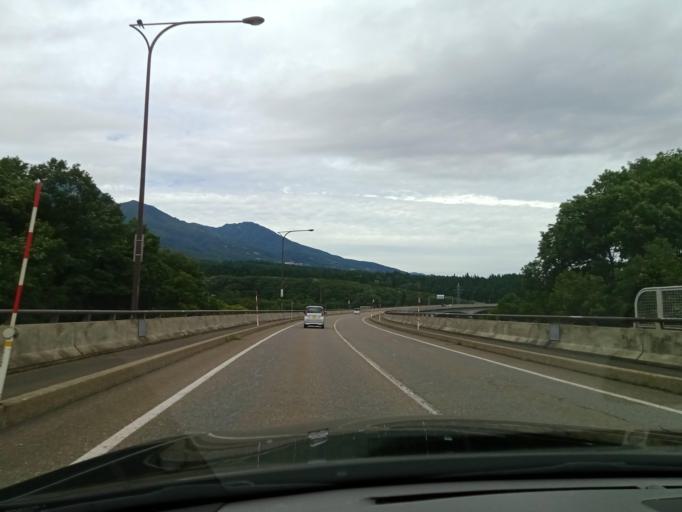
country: JP
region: Niigata
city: Arai
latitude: 36.8511
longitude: 138.1936
